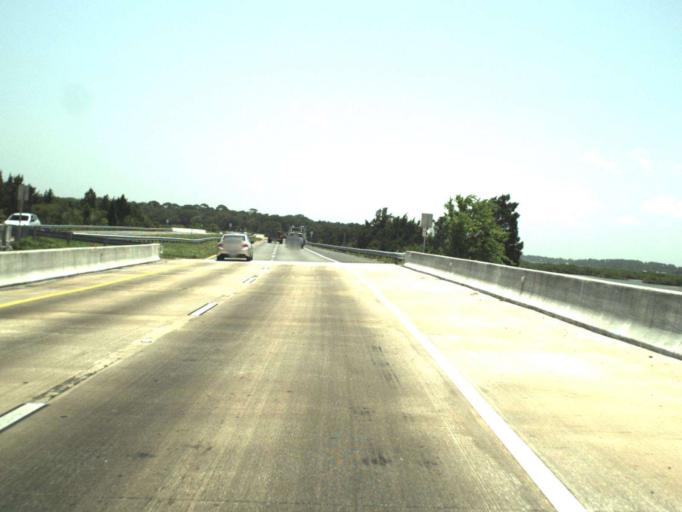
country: US
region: Florida
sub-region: Volusia County
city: Ponce Inlet
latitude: 29.0888
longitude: -80.9701
